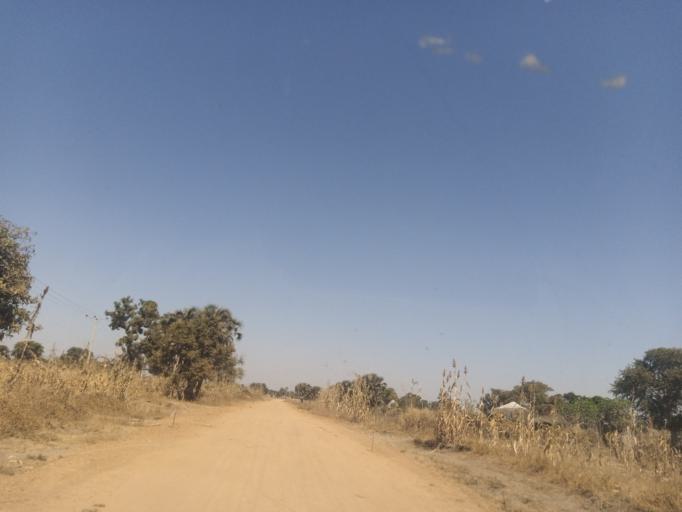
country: NG
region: Adamawa
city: Yola
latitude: 9.2896
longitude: 12.8850
